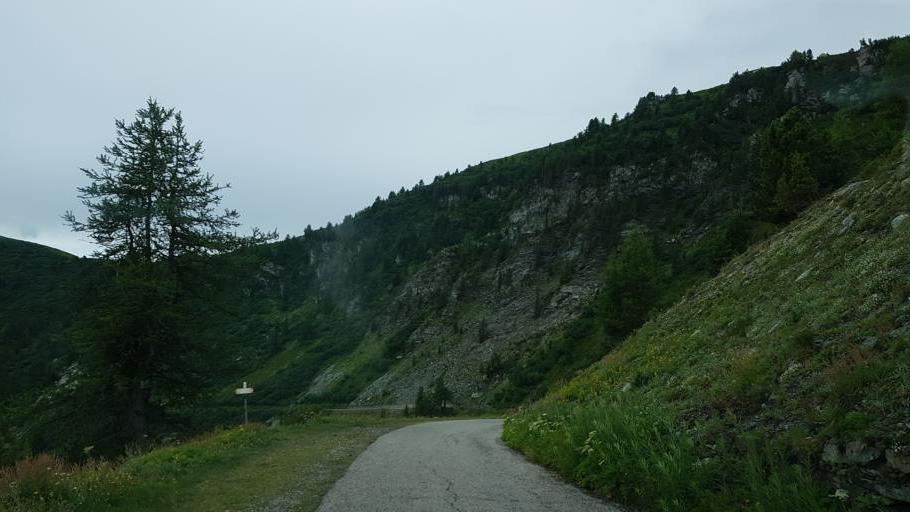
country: IT
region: Piedmont
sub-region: Provincia di Cuneo
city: Serre
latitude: 44.5506
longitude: 7.1266
